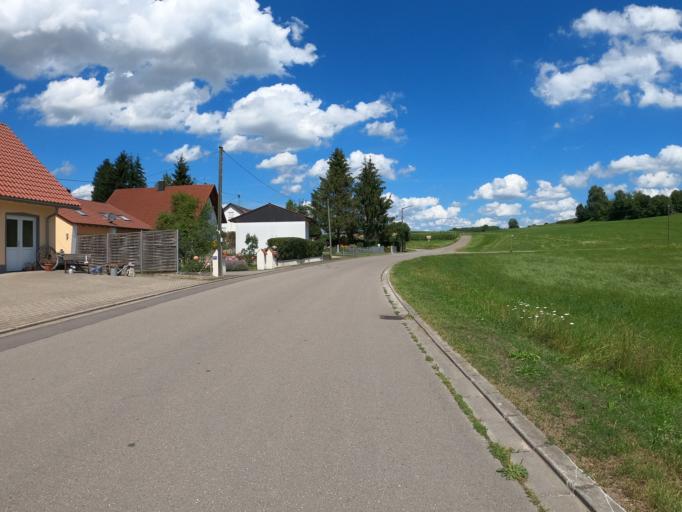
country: DE
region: Bavaria
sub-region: Swabia
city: Pfaffenhofen an der Roth
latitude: 48.4011
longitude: 10.1867
